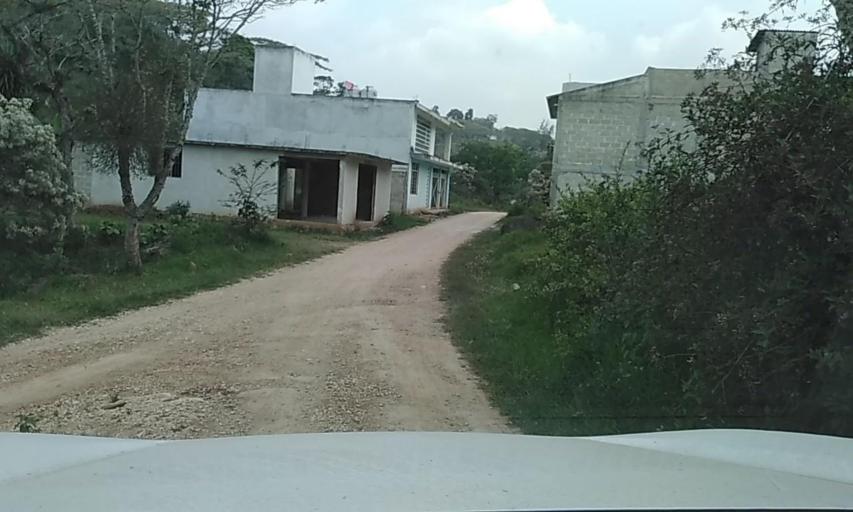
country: MX
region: Veracruz
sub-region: Xalapa
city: Fraccionamiento las Fuentes
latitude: 19.4900
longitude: -96.8965
